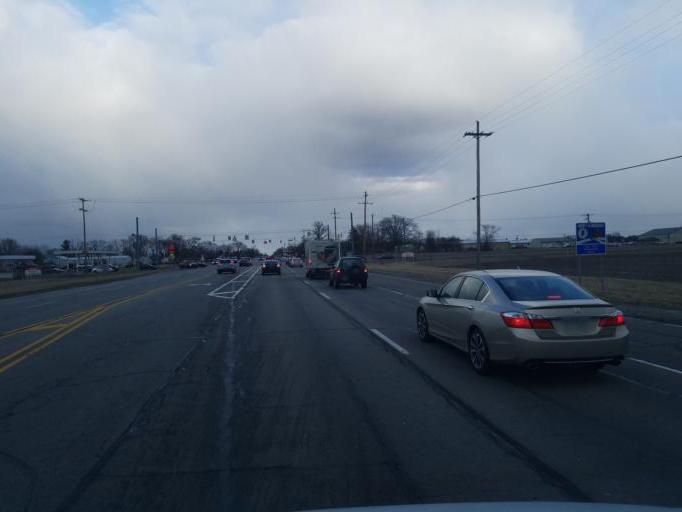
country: US
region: Indiana
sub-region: Marion County
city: Cumberland
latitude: 39.7785
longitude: -85.9160
